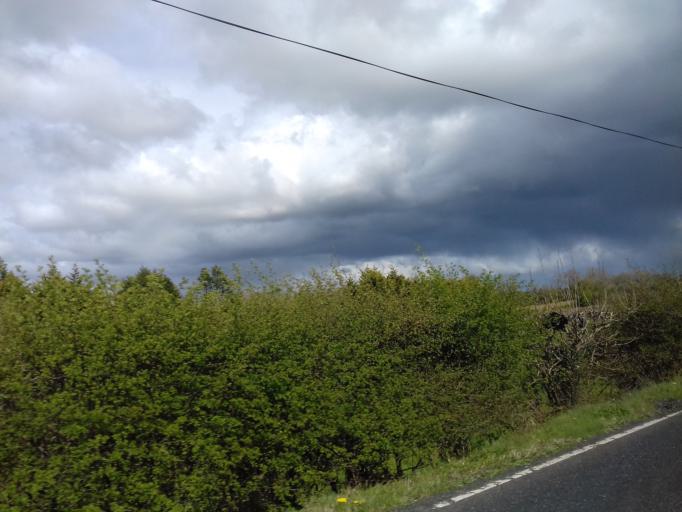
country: IE
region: Ulster
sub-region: County Donegal
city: Ballyshannon
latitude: 54.4700
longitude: -8.0582
